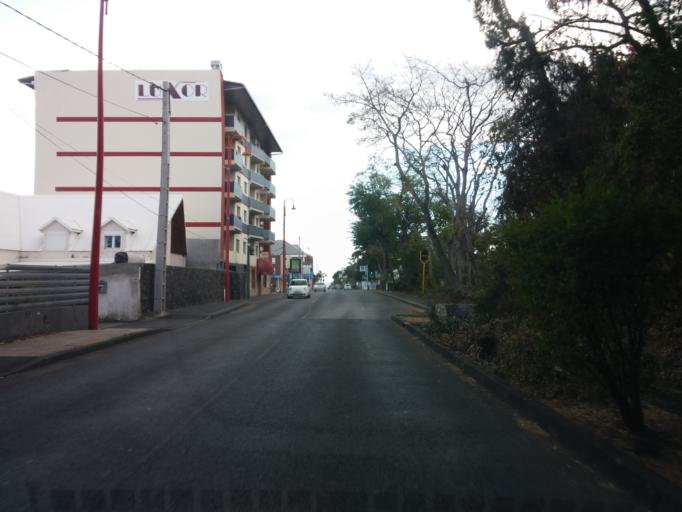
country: RE
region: Reunion
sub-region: Reunion
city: La Possession
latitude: -20.9336
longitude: 55.3346
